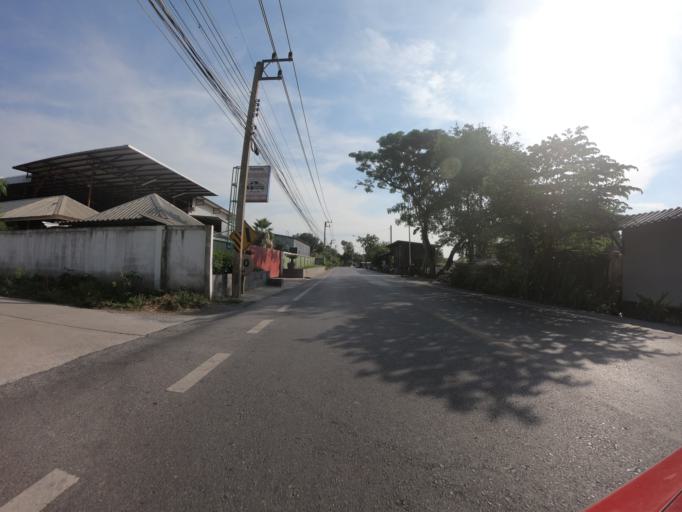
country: TH
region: Pathum Thani
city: Thanyaburi
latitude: 13.9777
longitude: 100.7289
